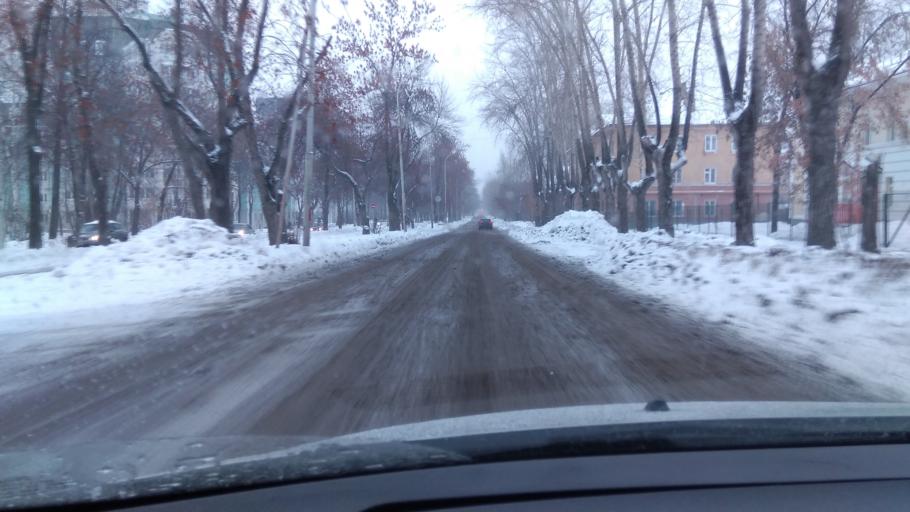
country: RU
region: Sverdlovsk
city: Yekaterinburg
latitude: 56.8964
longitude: 60.5817
